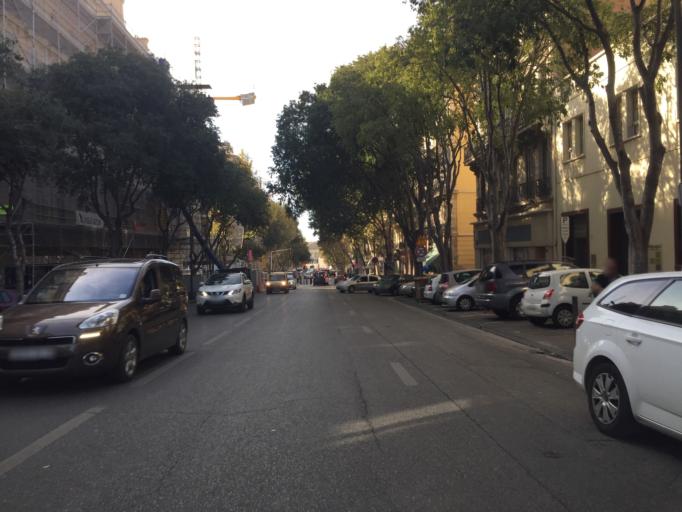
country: FR
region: Provence-Alpes-Cote d'Azur
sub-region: Departement des Bouches-du-Rhone
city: Marseille 03
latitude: 43.3023
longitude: 5.3703
